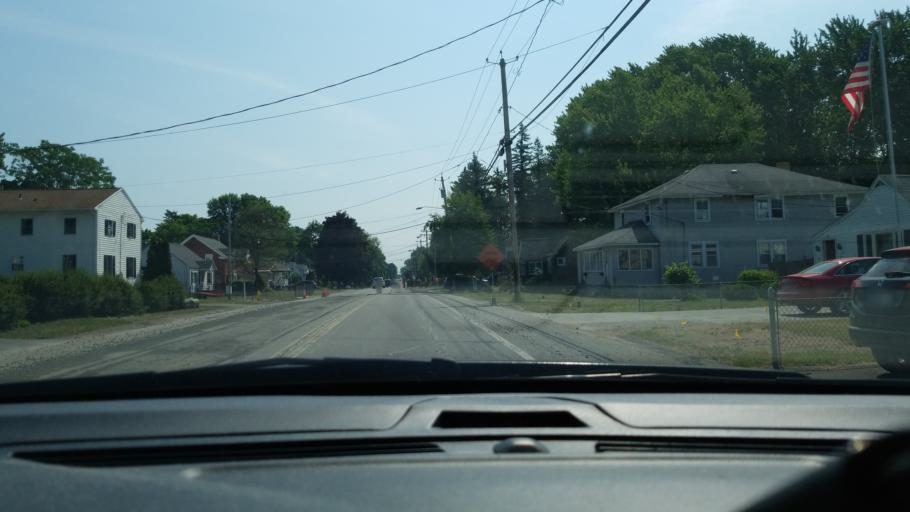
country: US
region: New York
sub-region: Onondaga County
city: Mattydale
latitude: 43.0981
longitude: -76.1382
